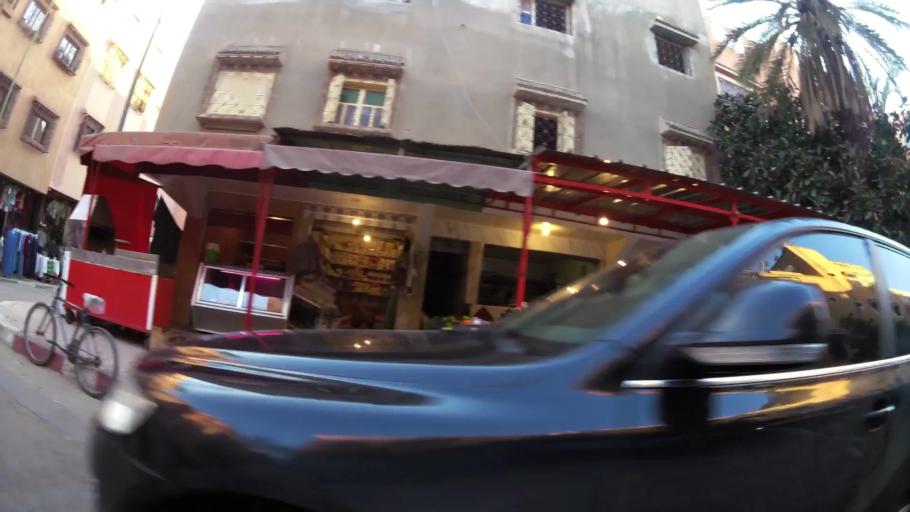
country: MA
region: Marrakech-Tensift-Al Haouz
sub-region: Marrakech
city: Marrakesh
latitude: 31.6381
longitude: -8.0364
